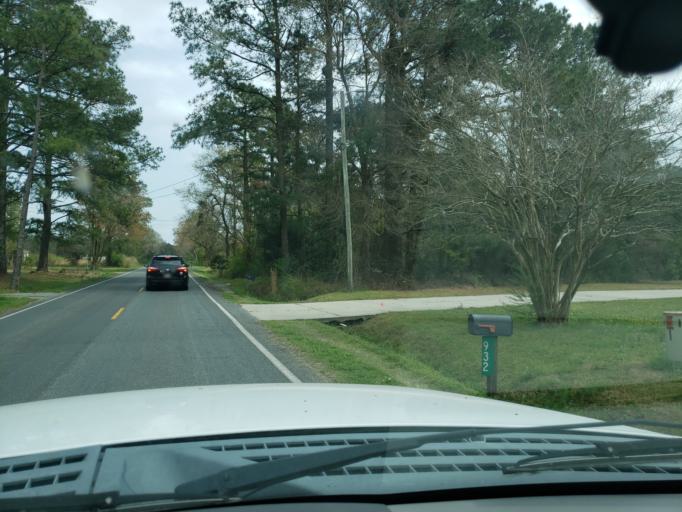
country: US
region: North Carolina
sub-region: Duplin County
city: Beulaville
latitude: 34.7747
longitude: -77.8141
